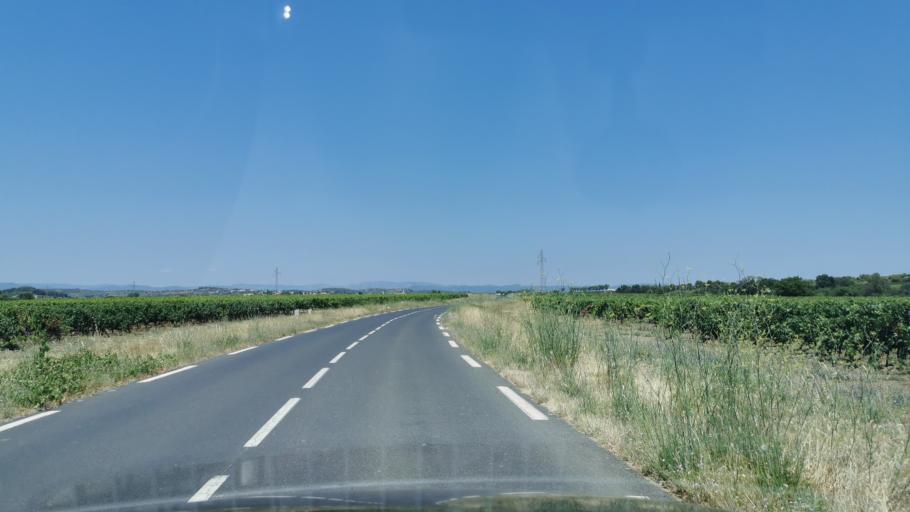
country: FR
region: Languedoc-Roussillon
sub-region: Departement de l'Herault
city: Maureilhan
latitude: 43.3690
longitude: 3.1143
